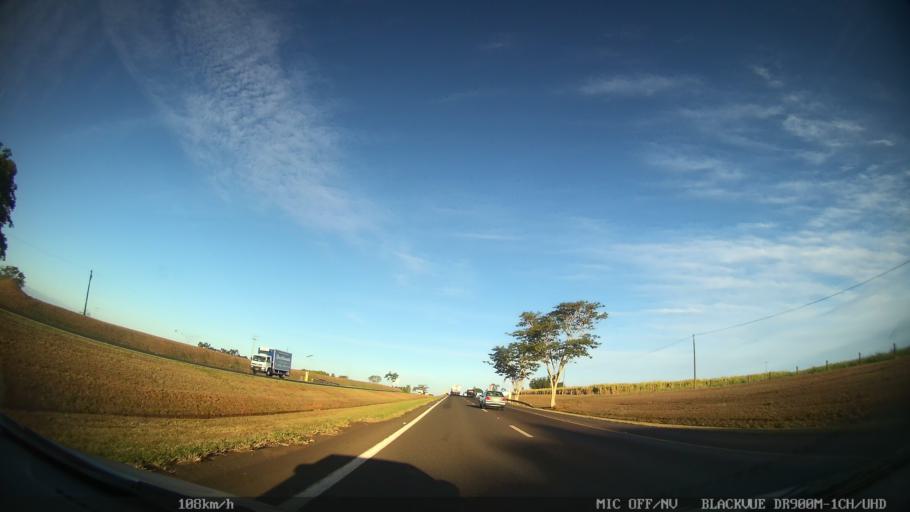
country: BR
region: Sao Paulo
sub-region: Urupes
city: Urupes
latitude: -21.0164
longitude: -49.1727
